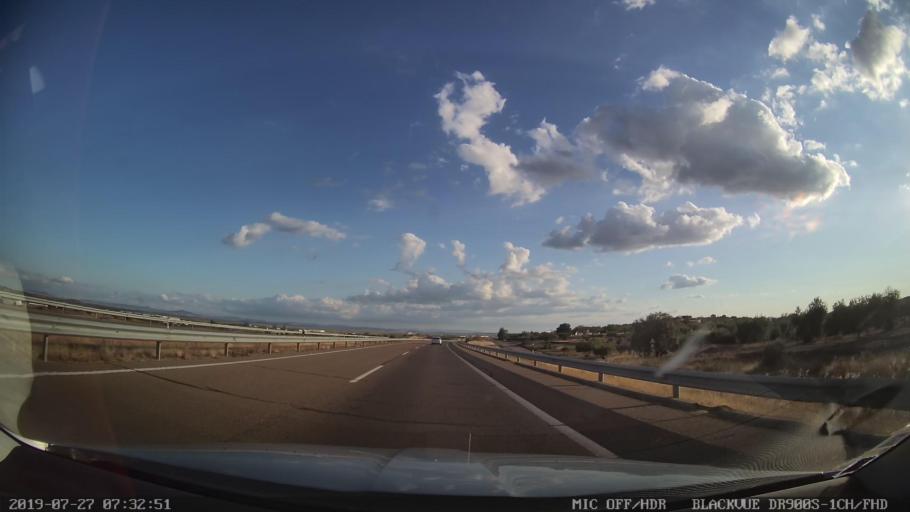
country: ES
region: Extremadura
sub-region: Provincia de Caceres
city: Miajadas
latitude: 39.1518
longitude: -5.9282
